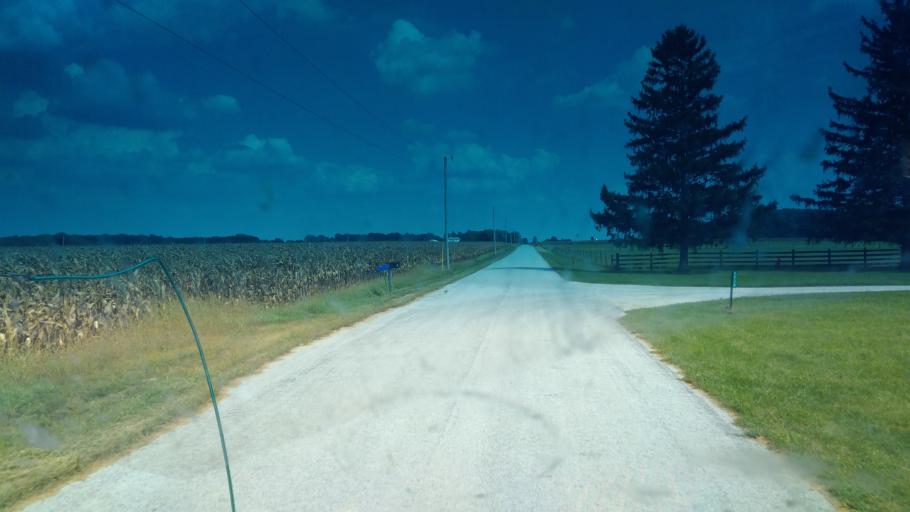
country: US
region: Ohio
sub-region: Hardin County
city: Kenton
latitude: 40.6598
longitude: -83.7107
